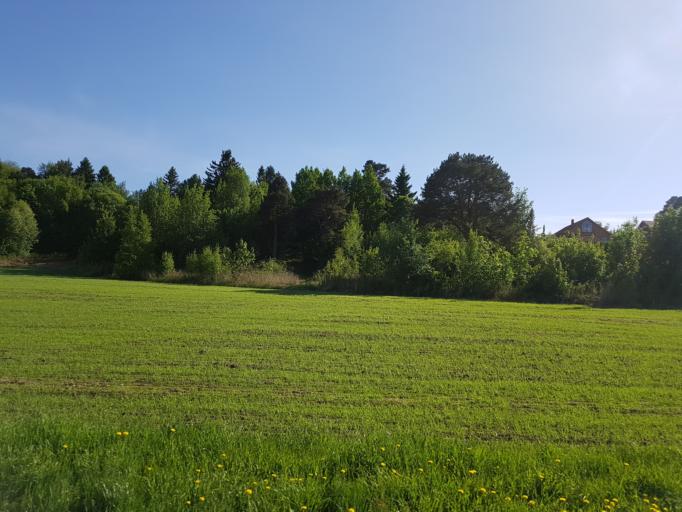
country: NO
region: Sor-Trondelag
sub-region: Trondheim
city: Trondheim
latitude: 63.4257
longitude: 10.5095
